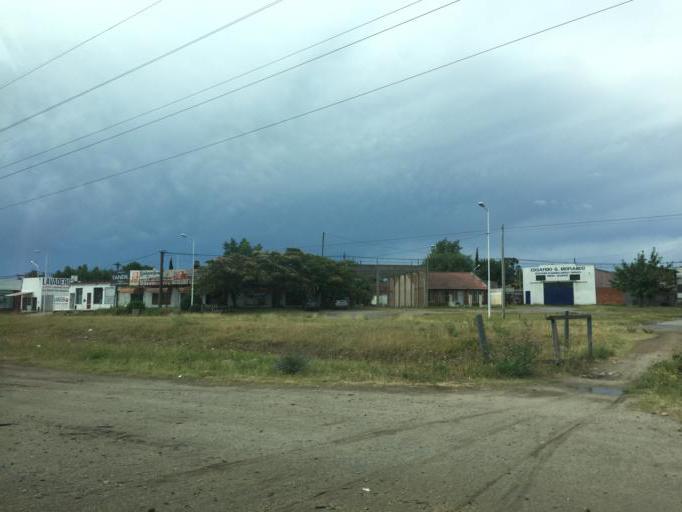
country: AR
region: Buenos Aires
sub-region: Partido de Tandil
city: Tandil
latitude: -37.3100
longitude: -59.1161
